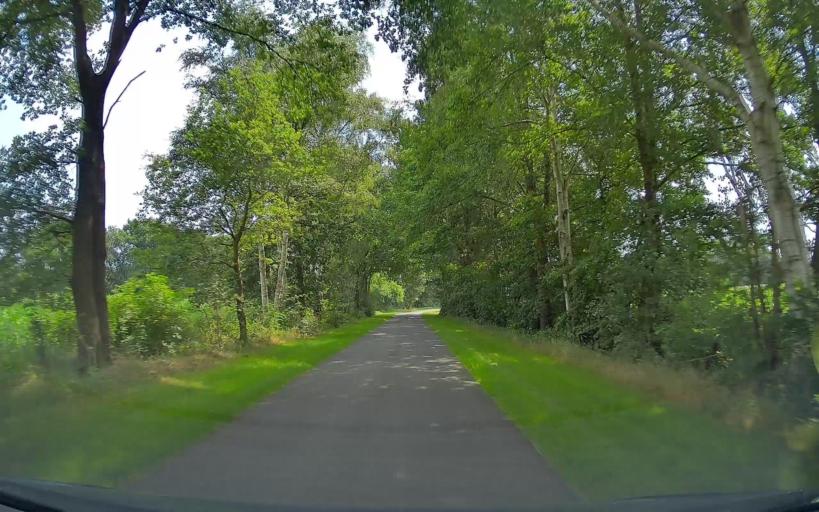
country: DE
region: Lower Saxony
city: Friesoythe
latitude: 52.9911
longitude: 7.8791
